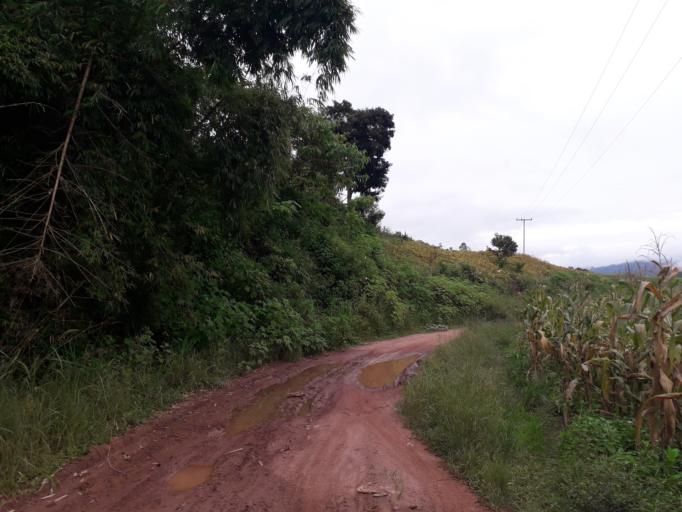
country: CN
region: Yunnan
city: Menglie
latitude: 22.2494
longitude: 101.6058
